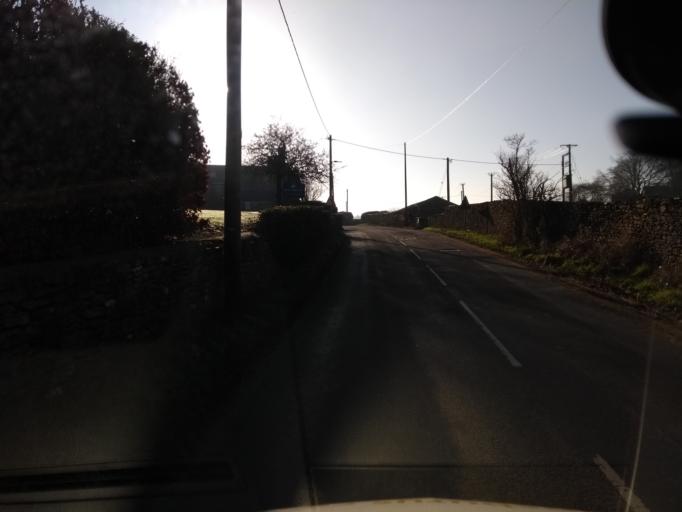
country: GB
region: England
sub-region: Somerset
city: Bruton
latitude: 51.1095
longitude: -2.4492
